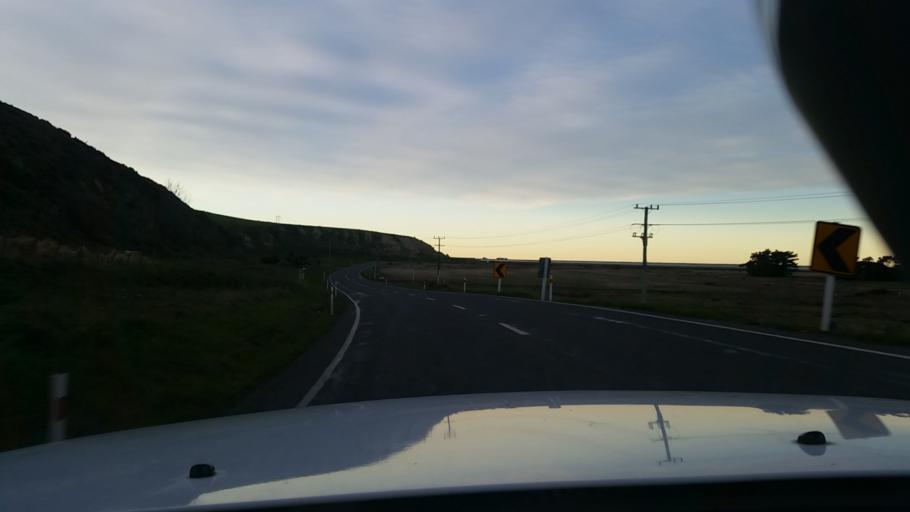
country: NZ
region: Canterbury
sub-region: Selwyn District
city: Lincoln
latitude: -43.7491
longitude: 172.6135
